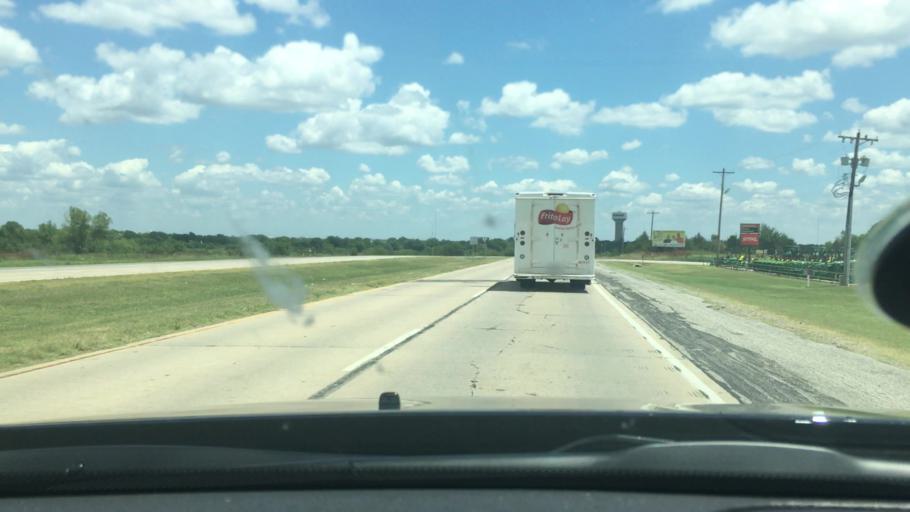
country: US
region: Oklahoma
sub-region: Carter County
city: Lone Grove
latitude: 34.1728
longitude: -97.2100
